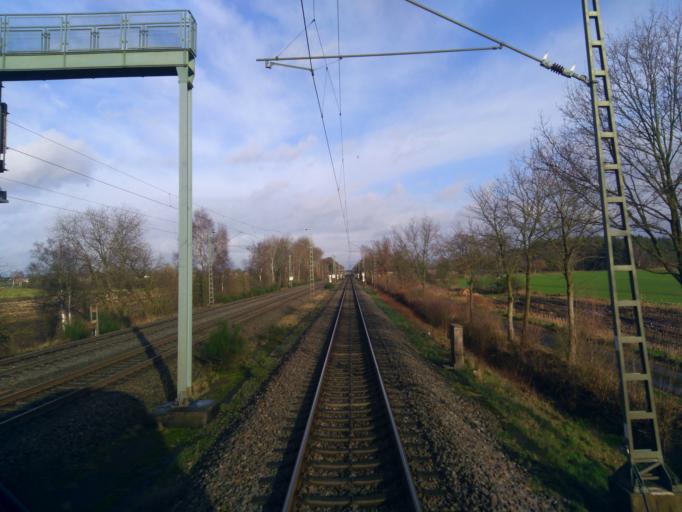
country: DE
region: Lower Saxony
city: Scheessel
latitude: 53.1517
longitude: 9.4780
